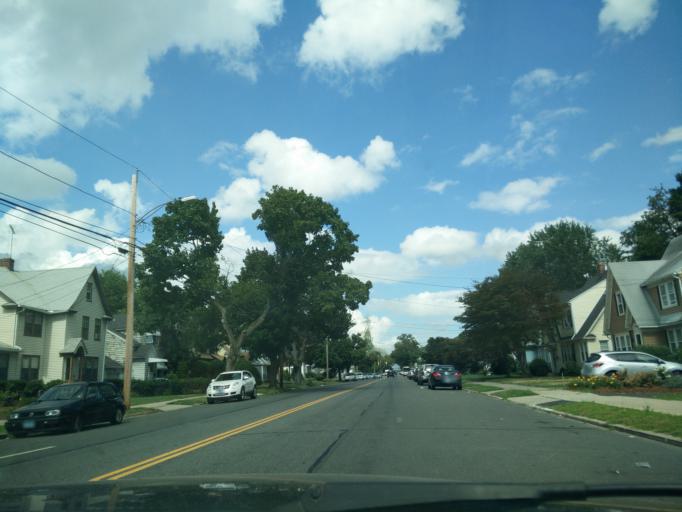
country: US
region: Connecticut
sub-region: Fairfield County
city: Bridgeport
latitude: 41.1907
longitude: -73.2126
